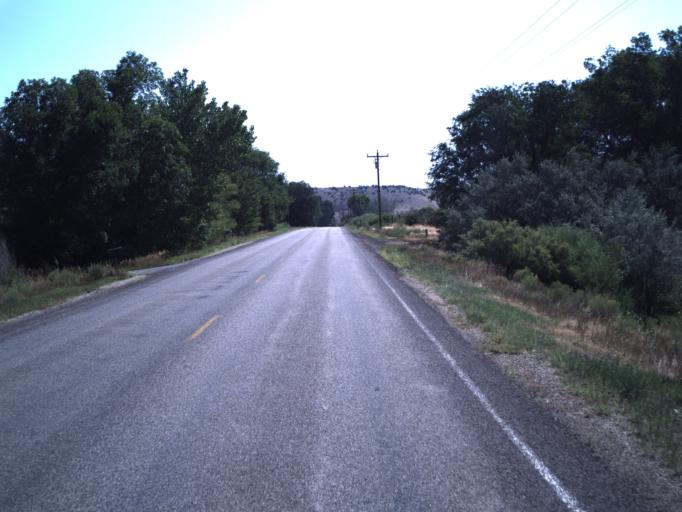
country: US
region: Utah
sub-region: Duchesne County
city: Duchesne
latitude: 40.2708
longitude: -110.4373
